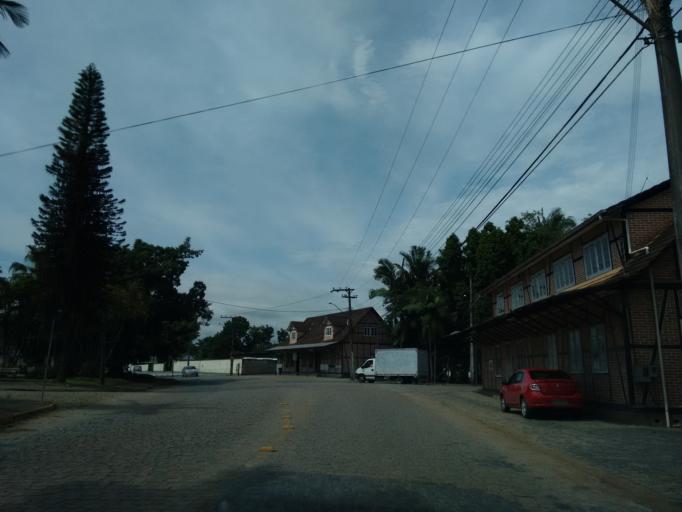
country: BR
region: Santa Catarina
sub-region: Pomerode
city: Pomerode
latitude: -26.7068
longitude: -49.1645
